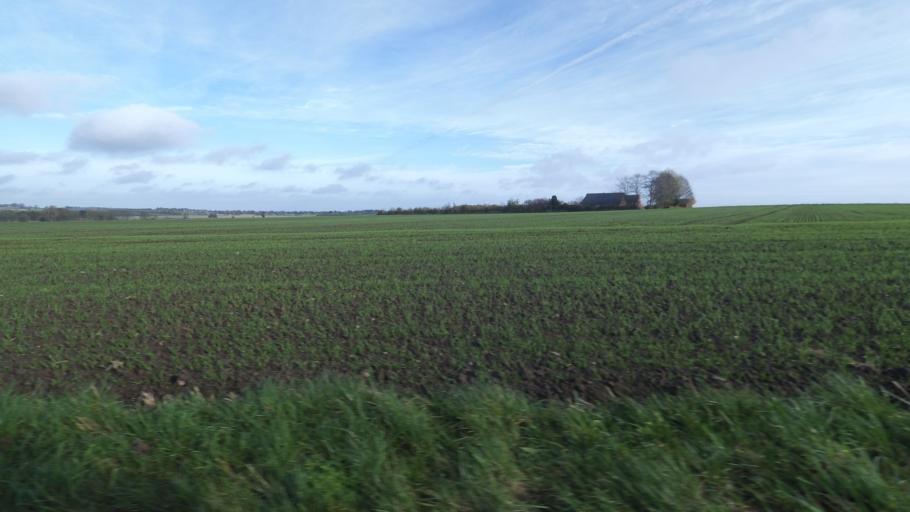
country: DK
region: Central Jutland
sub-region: Odder Kommune
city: Odder
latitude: 55.9565
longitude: 10.2384
